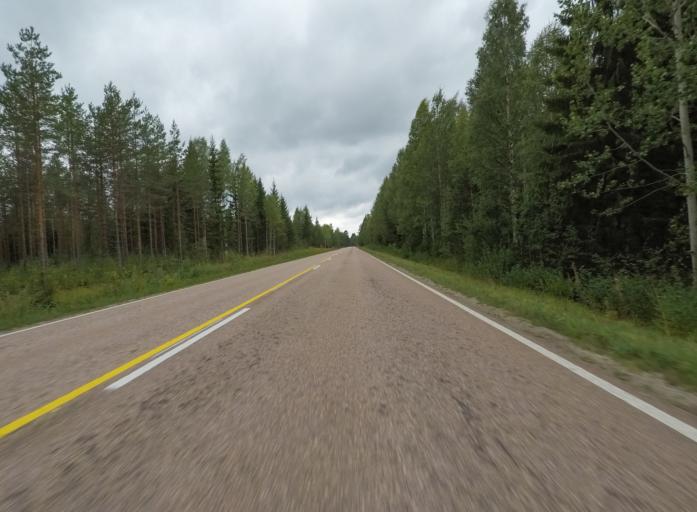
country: FI
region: Central Finland
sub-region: Jyvaeskylae
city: Hankasalmi
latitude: 62.3590
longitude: 26.5535
